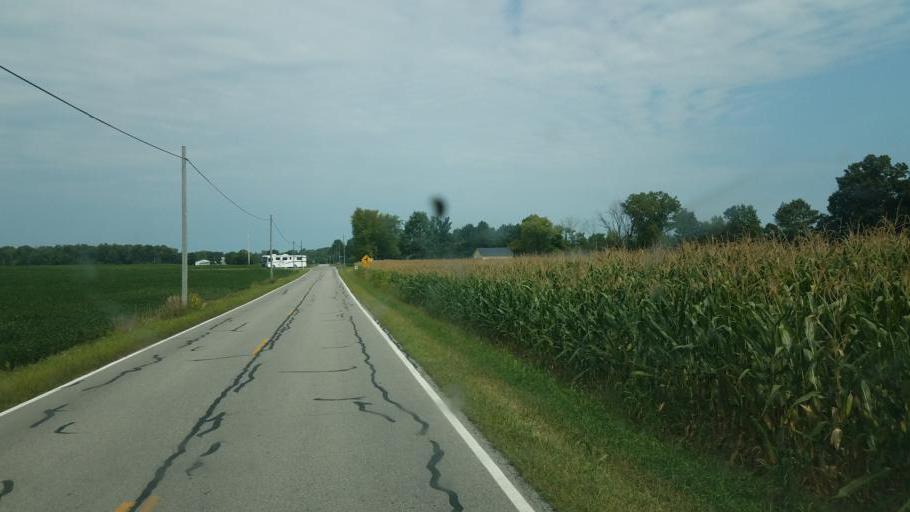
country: US
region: Ohio
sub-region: Marion County
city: Marion
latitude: 40.5184
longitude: -83.0628
